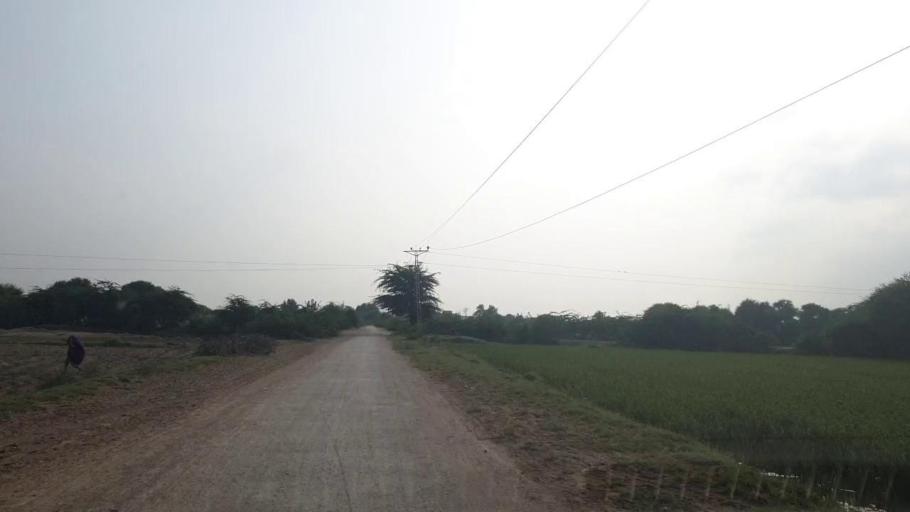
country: PK
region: Sindh
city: Badin
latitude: 24.6144
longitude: 68.6861
